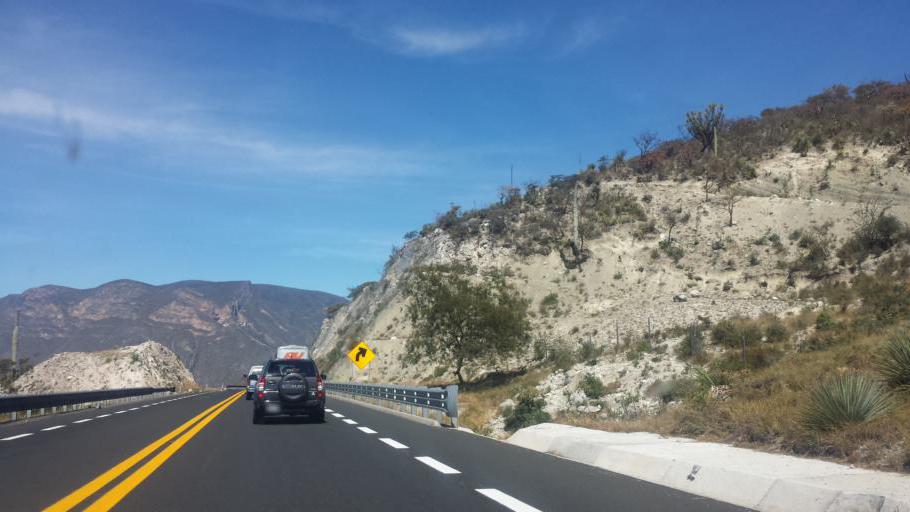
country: MX
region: Puebla
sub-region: San Jose Miahuatlan
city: San Pedro Tetitlan
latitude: 18.0833
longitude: -97.3508
